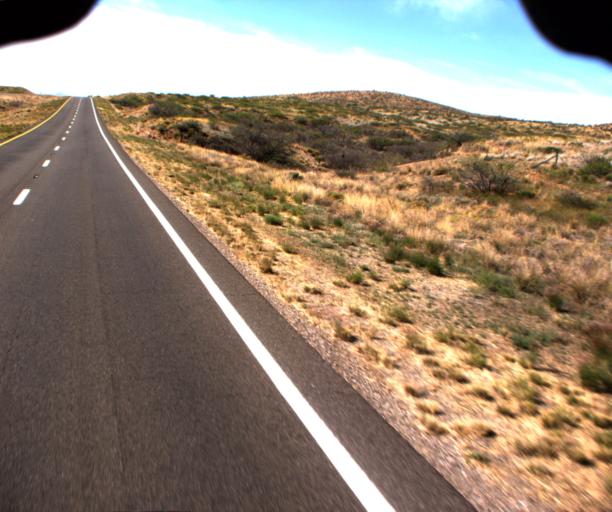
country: US
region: Arizona
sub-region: Graham County
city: Swift Trail Junction
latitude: 32.5116
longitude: -109.6742
